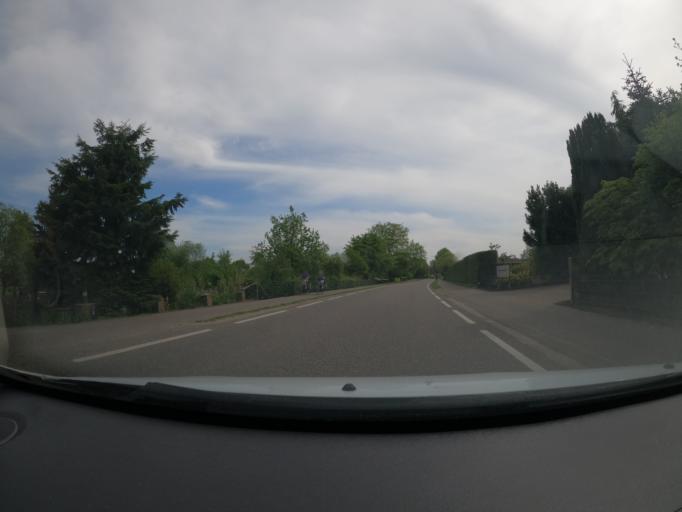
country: NL
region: Gelderland
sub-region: Gemeente Montferland
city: s-Heerenberg
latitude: 51.9124
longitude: 6.2552
